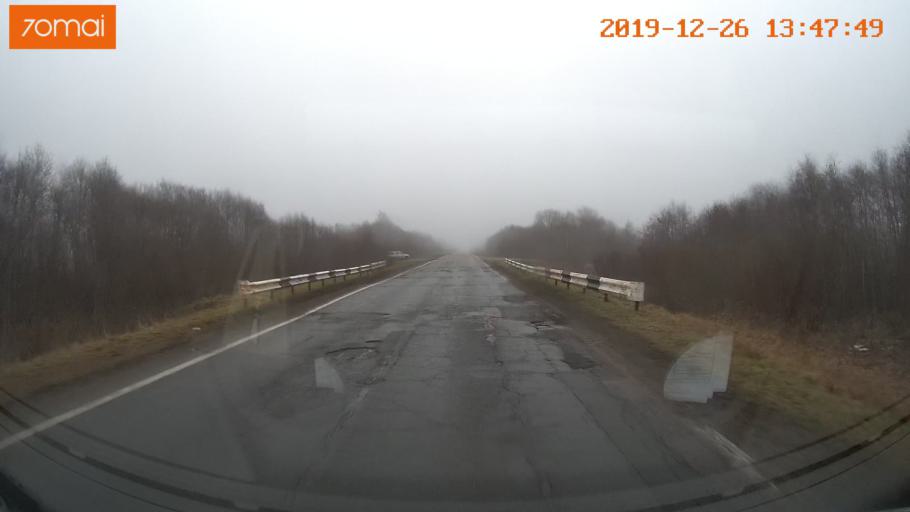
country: RU
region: Vologda
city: Sheksna
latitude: 58.6818
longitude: 38.5387
